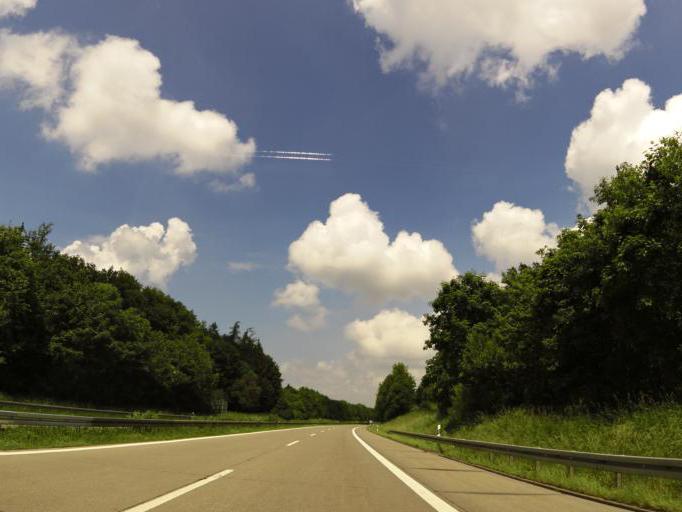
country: DE
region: Baden-Wuerttemberg
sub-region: Regierungsbezirk Stuttgart
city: Westhausen
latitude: 48.8432
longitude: 10.1988
